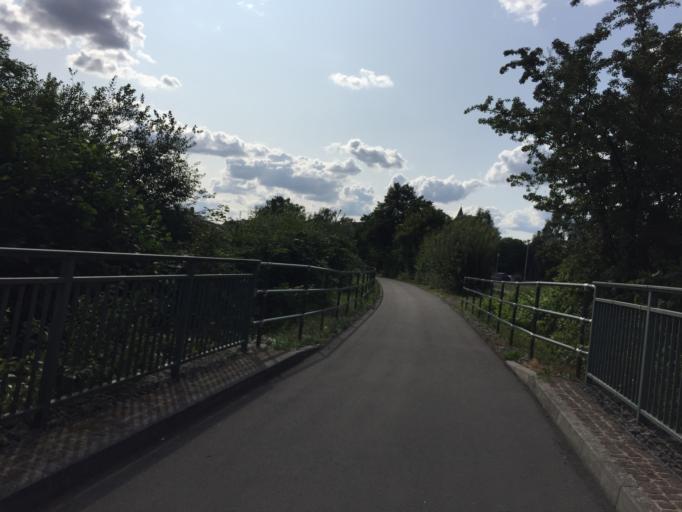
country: DE
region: Hesse
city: Schwalmstadt
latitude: 50.9127
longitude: 9.1947
